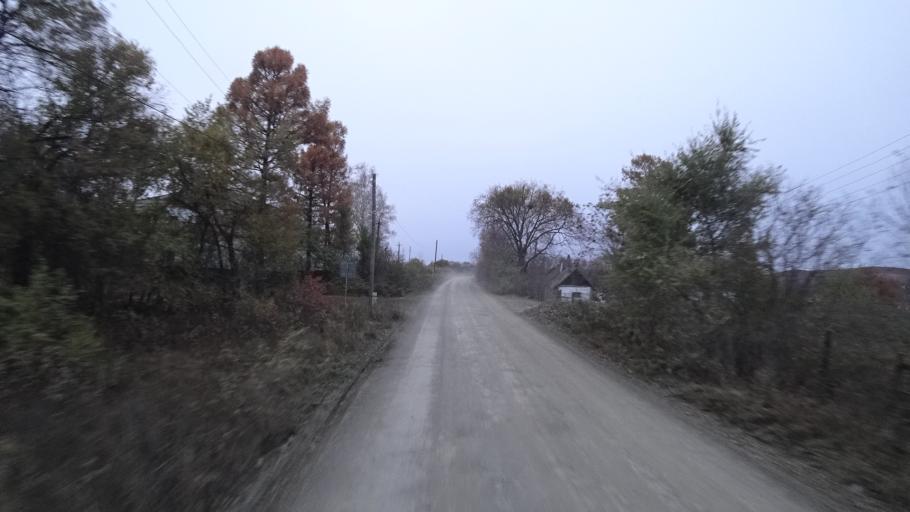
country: RU
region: Khabarovsk Krai
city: Amursk
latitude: 49.9015
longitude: 136.1424
